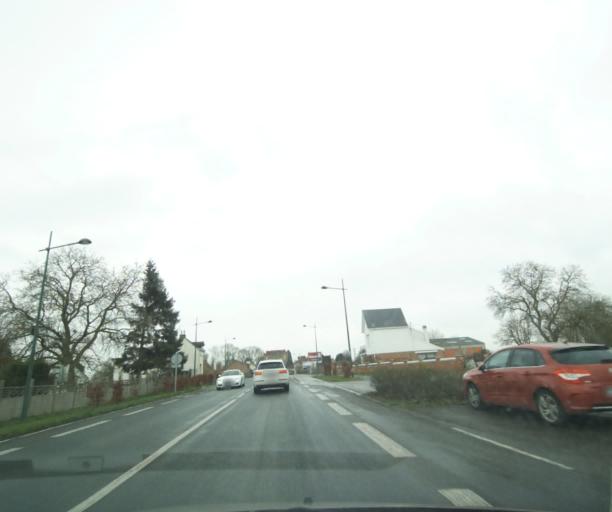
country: FR
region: Nord-Pas-de-Calais
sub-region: Departement du Nord
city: Haulchin
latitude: 50.3206
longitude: 3.4276
